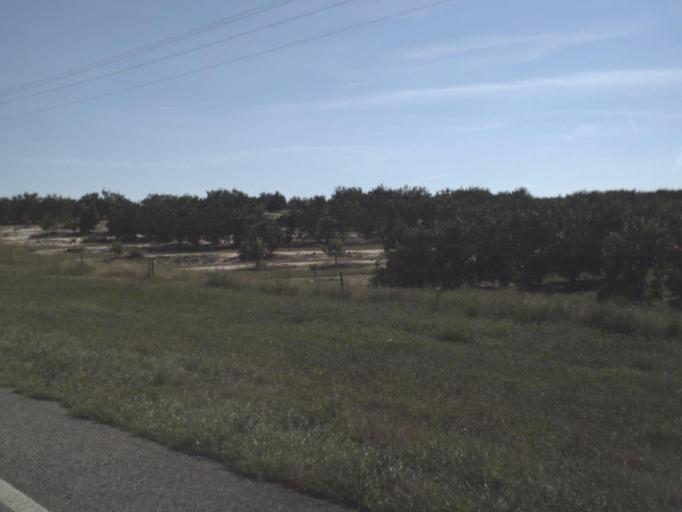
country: US
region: Florida
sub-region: Highlands County
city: Lake Placid
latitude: 27.3657
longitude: -81.3964
